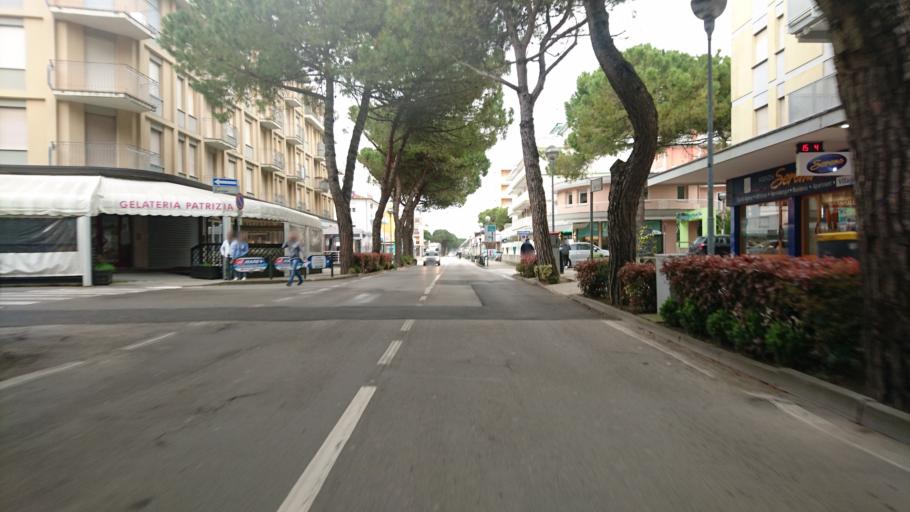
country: IT
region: Veneto
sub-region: Provincia di Venezia
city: Bibione
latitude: 45.6353
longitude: 13.0615
